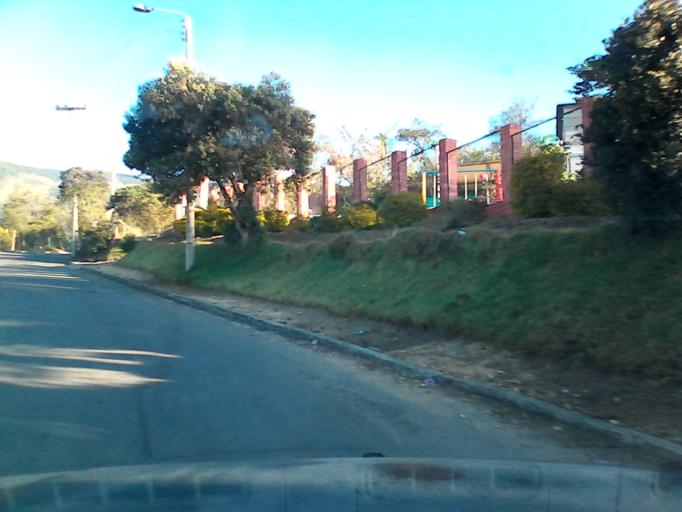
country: CO
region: Boyaca
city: Duitama
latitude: 5.8575
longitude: -73.0257
